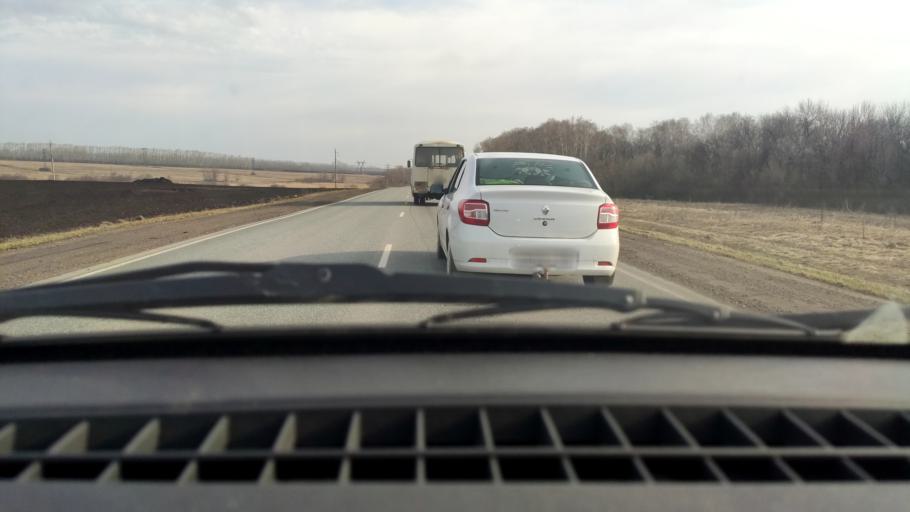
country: RU
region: Bashkortostan
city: Chishmy
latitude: 54.5056
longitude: 55.2885
